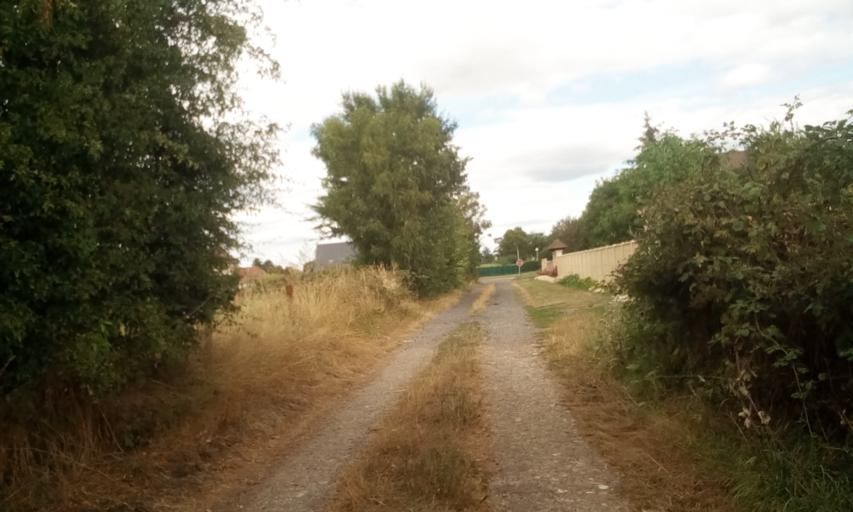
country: FR
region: Lower Normandy
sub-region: Departement du Calvados
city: Troarn
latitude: 49.1650
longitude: -0.1833
